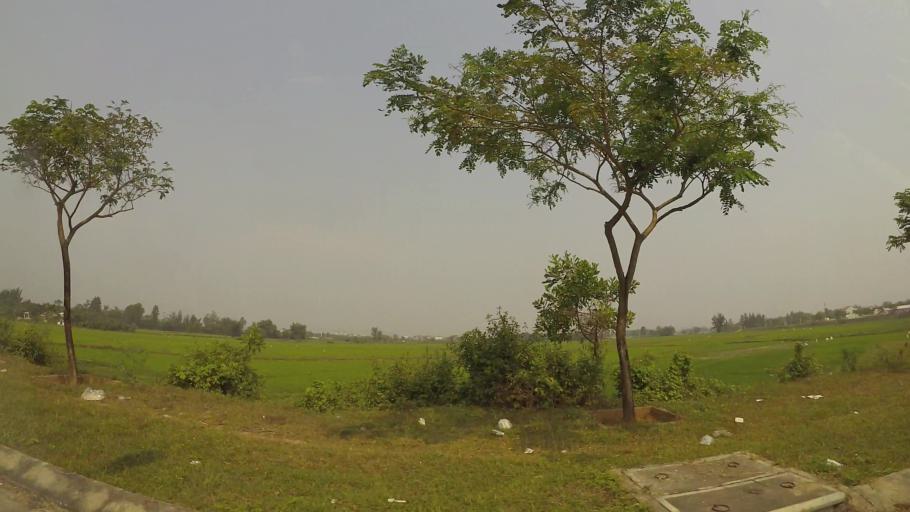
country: VN
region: Da Nang
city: Cam Le
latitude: 15.9711
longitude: 108.2216
